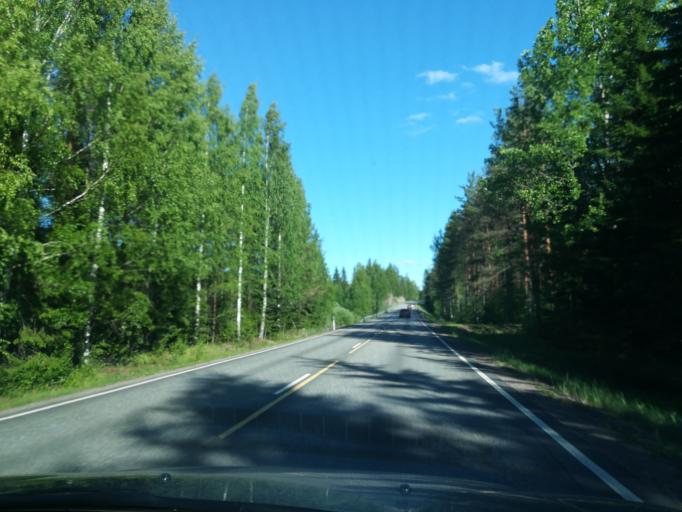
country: FI
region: South Karelia
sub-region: Imatra
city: Ruokolahti
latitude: 61.3644
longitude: 28.6922
